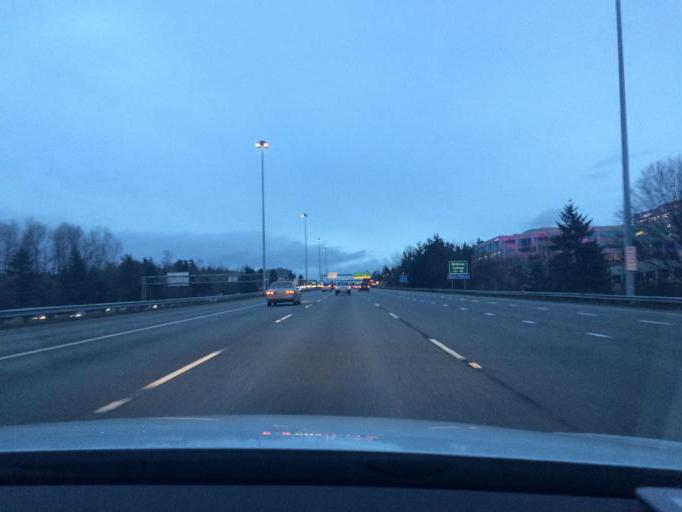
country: US
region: Washington
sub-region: King County
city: Newport
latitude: 47.5801
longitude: -122.1683
